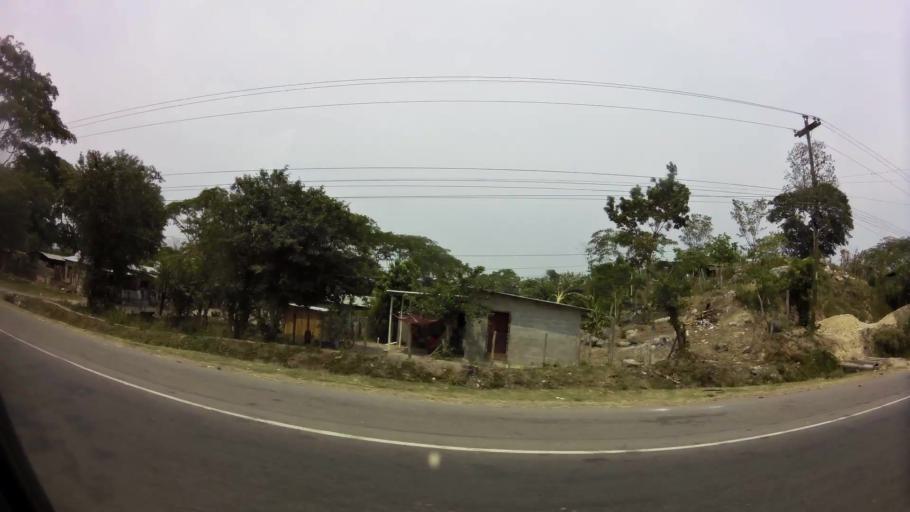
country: HN
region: Cortes
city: Nuevo Chamelecon
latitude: 15.3793
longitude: -87.9891
